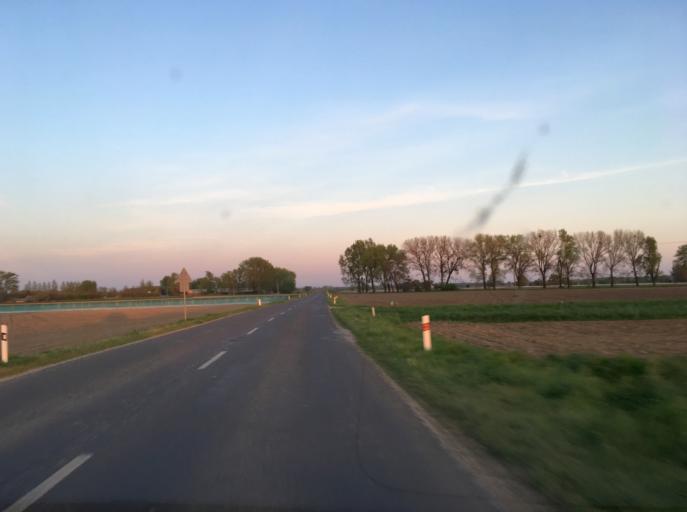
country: SK
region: Nitriansky
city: Kolarovo
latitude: 47.9241
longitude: 18.0286
